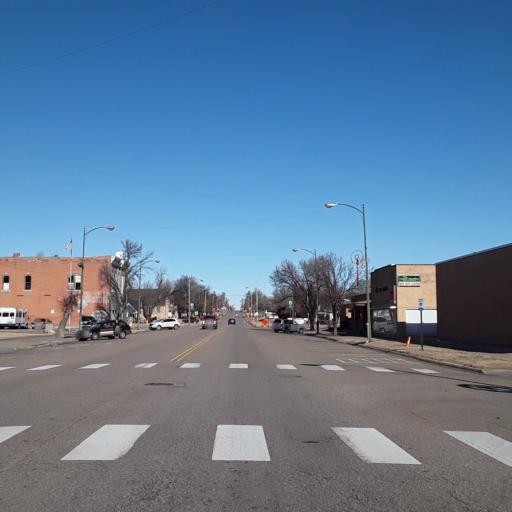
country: US
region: Kansas
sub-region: Pawnee County
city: Larned
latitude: 38.1821
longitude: -99.0982
